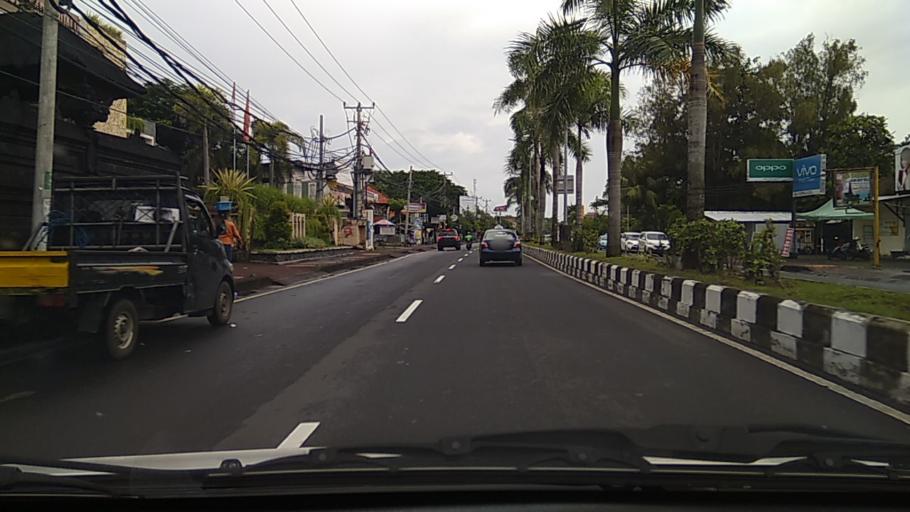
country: ID
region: Bali
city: Bualu
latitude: -8.7975
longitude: 115.2209
